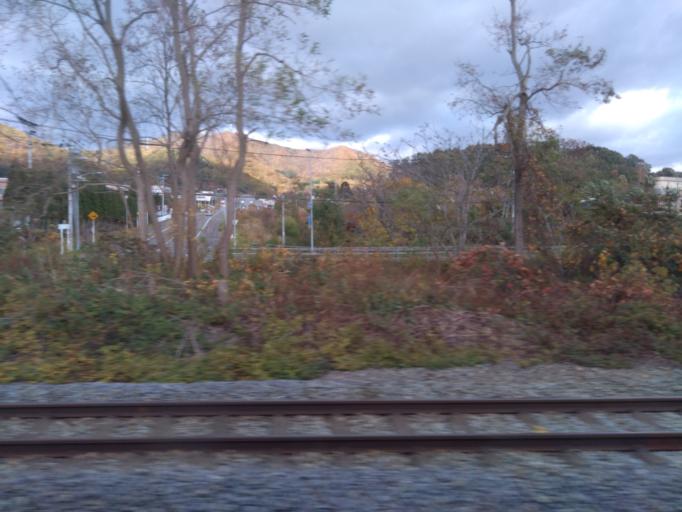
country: JP
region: Hokkaido
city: Date
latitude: 42.5828
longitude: 140.7132
